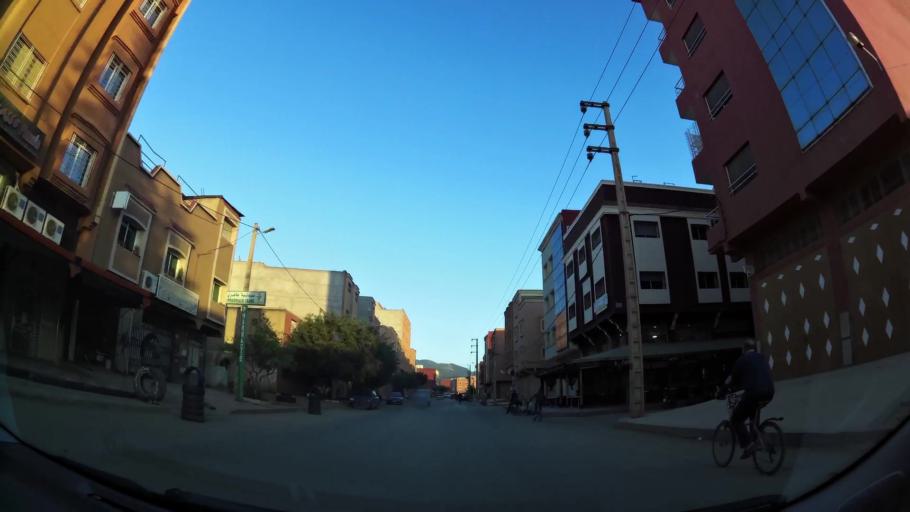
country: MA
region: Oriental
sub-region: Berkane-Taourirt
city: Berkane
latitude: 34.9173
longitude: -2.3244
